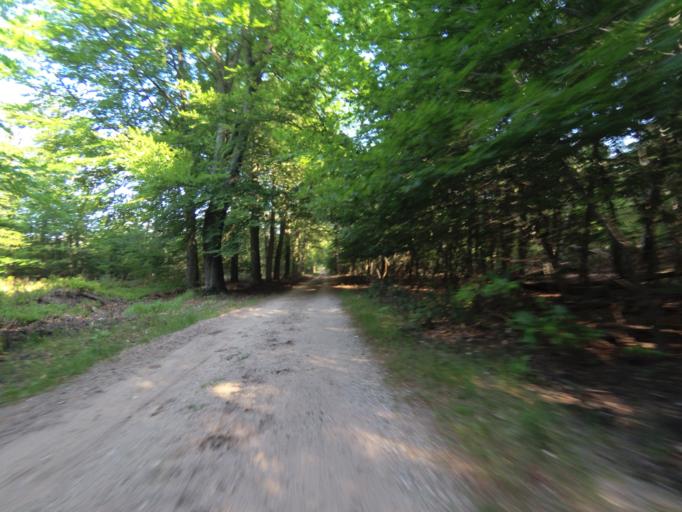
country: NL
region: Gelderland
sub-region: Gemeente Apeldoorn
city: Beekbergen
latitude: 52.1663
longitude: 5.8724
